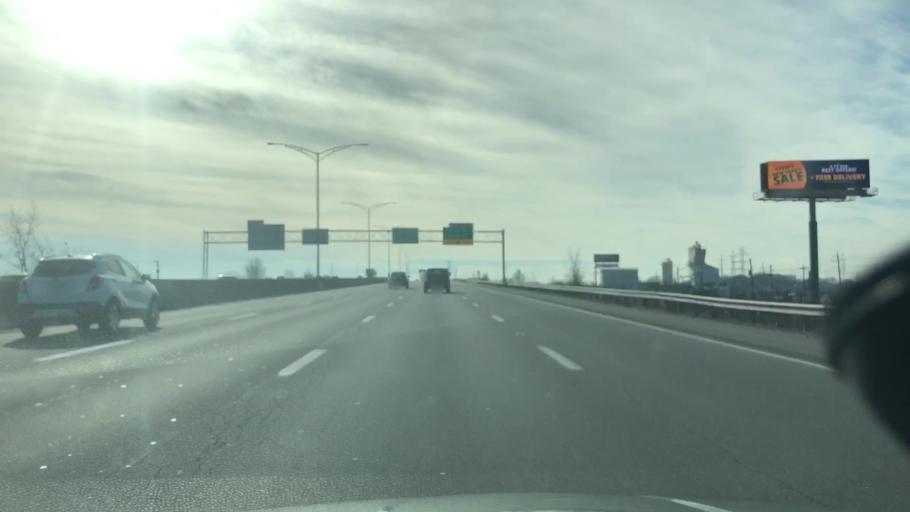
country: US
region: Ohio
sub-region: Cuyahoga County
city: Brook Park
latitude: 41.4098
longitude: -81.8181
